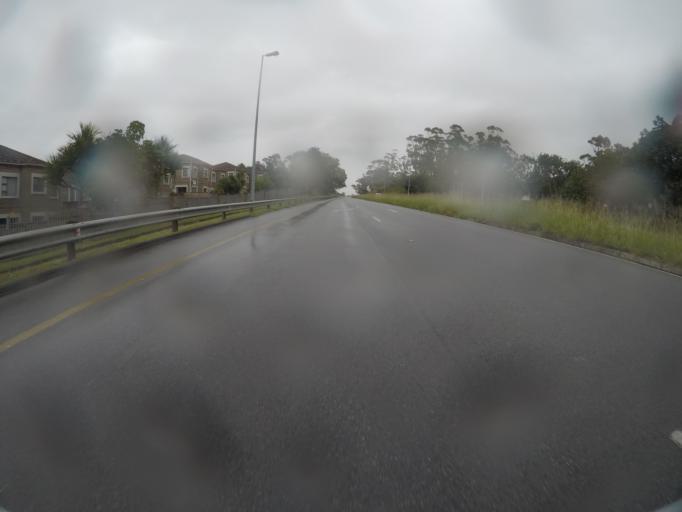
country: ZA
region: Eastern Cape
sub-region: Buffalo City Metropolitan Municipality
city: East London
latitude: -32.9598
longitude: 27.9172
